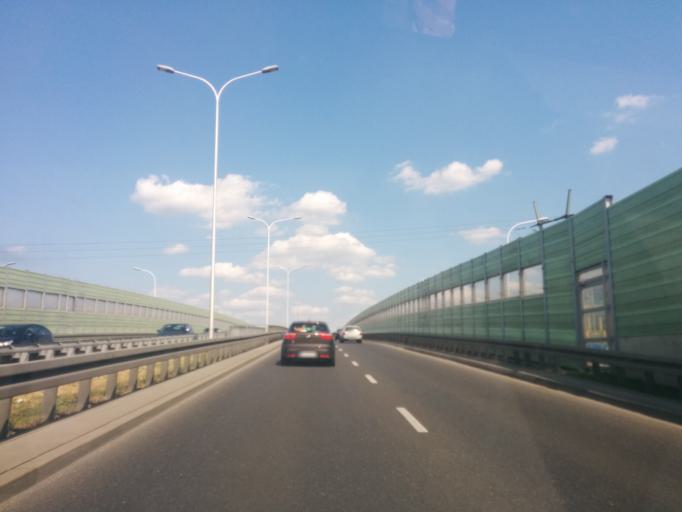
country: PL
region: Masovian Voivodeship
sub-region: Warszawa
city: Bialoleka
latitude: 52.3150
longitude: 20.9765
